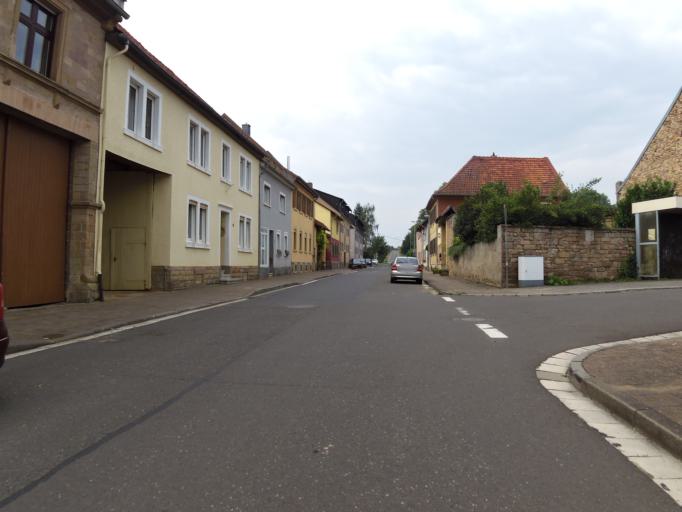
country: DE
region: Rheinland-Pfalz
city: Furfeld
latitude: 49.7763
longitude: 7.8889
